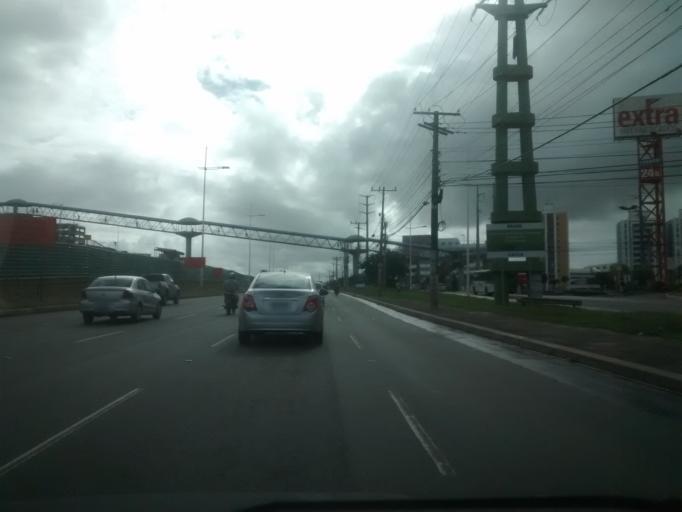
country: BR
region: Bahia
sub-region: Salvador
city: Salvador
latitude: -12.9635
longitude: -38.4349
